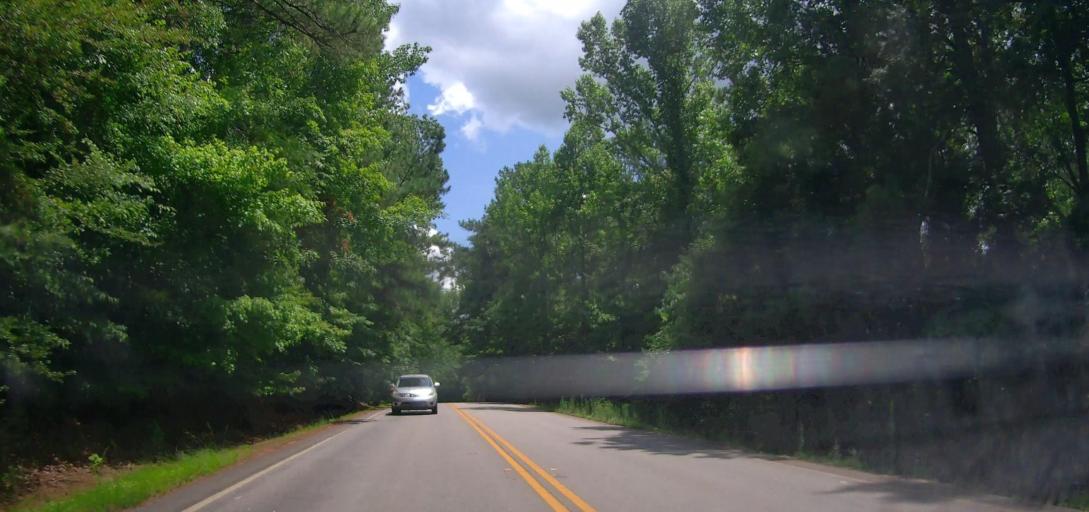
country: US
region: Georgia
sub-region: Troup County
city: Hogansville
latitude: 33.1424
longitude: -84.8414
